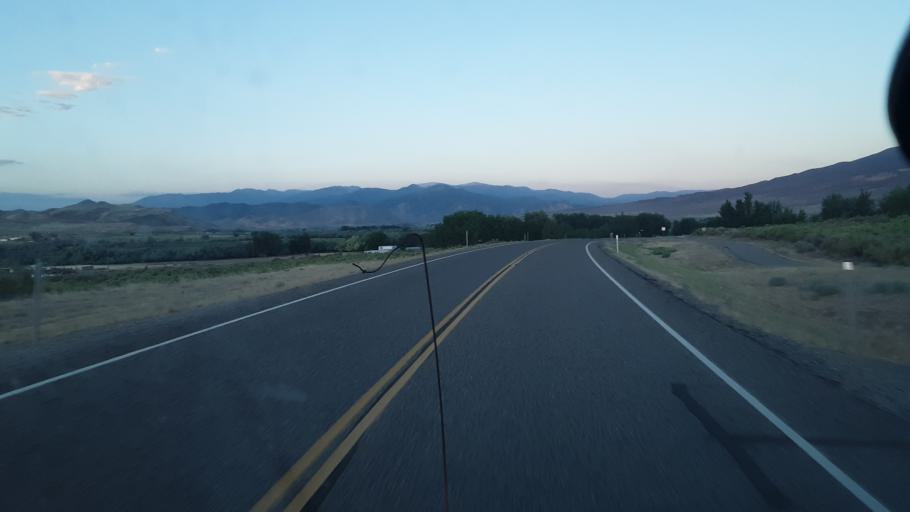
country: US
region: Utah
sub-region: Sevier County
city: Monroe
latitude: 38.6592
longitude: -112.1778
